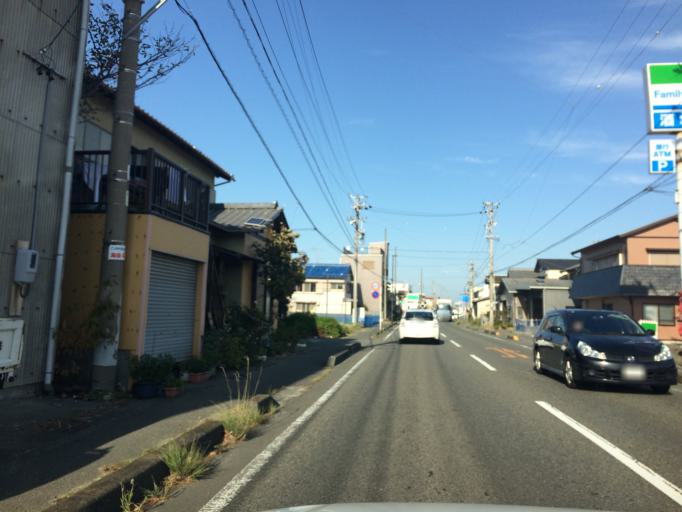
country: JP
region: Shizuoka
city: Sagara
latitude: 34.6798
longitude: 138.2006
